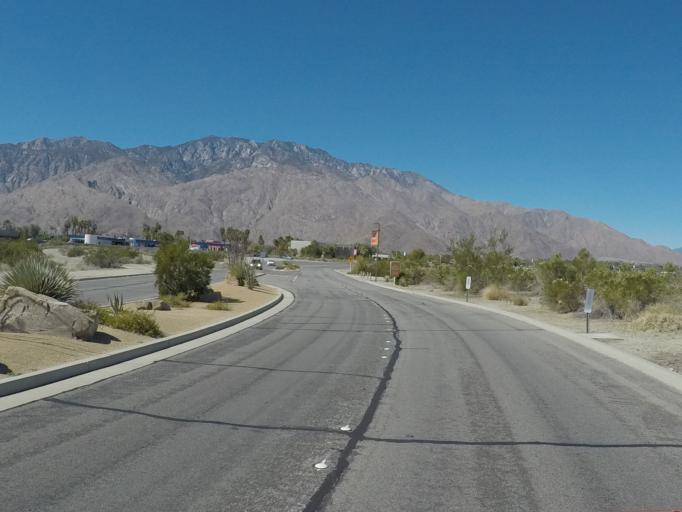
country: US
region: California
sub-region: Riverside County
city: Palm Springs
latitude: 33.8170
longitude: -116.4983
